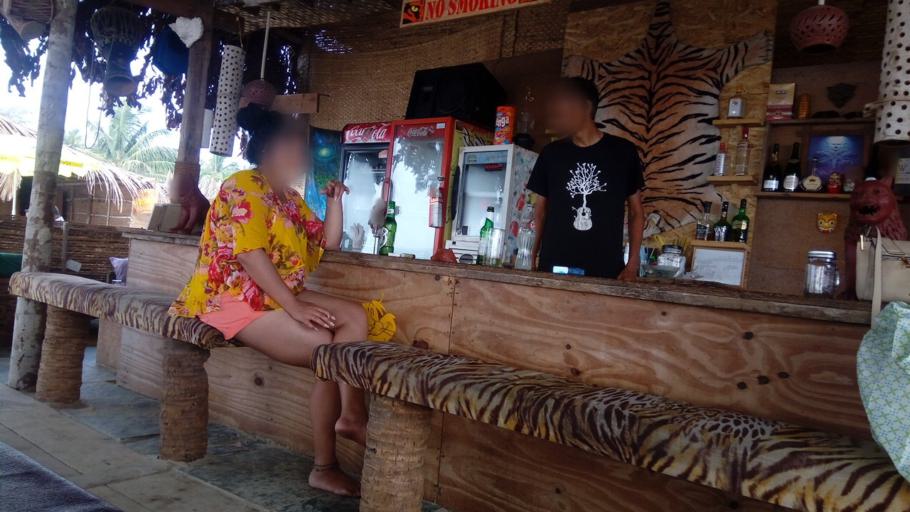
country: IN
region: Goa
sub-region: South Goa
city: Benaulim
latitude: 15.2586
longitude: 73.9185
